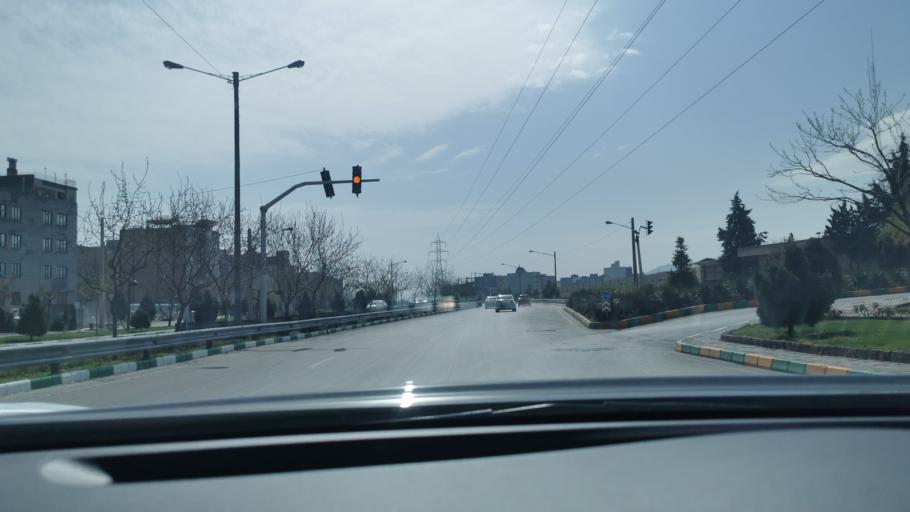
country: IR
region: Razavi Khorasan
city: Mashhad
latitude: 36.2852
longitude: 59.5401
